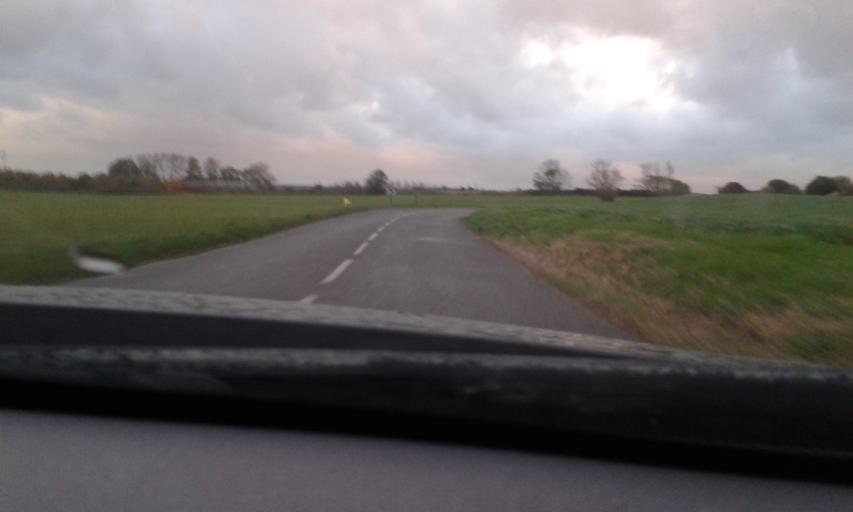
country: FR
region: Nord-Pas-de-Calais
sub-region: Departement du Pas-de-Calais
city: Hames-Boucres
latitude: 50.8709
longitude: 1.8229
